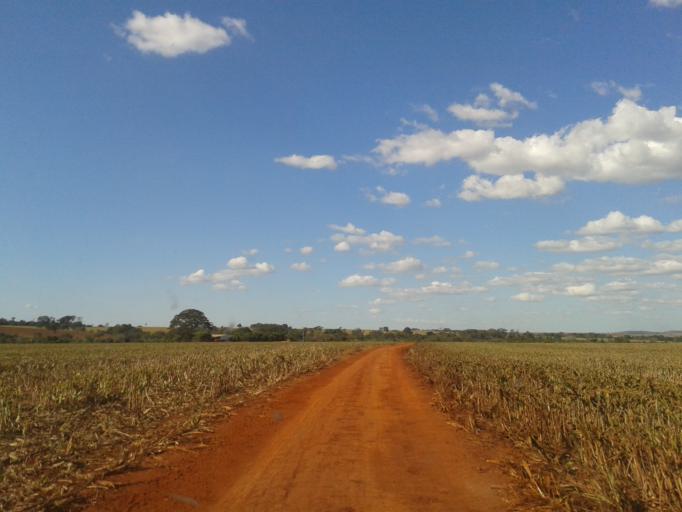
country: BR
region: Minas Gerais
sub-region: Centralina
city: Centralina
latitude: -18.5960
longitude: -49.2671
